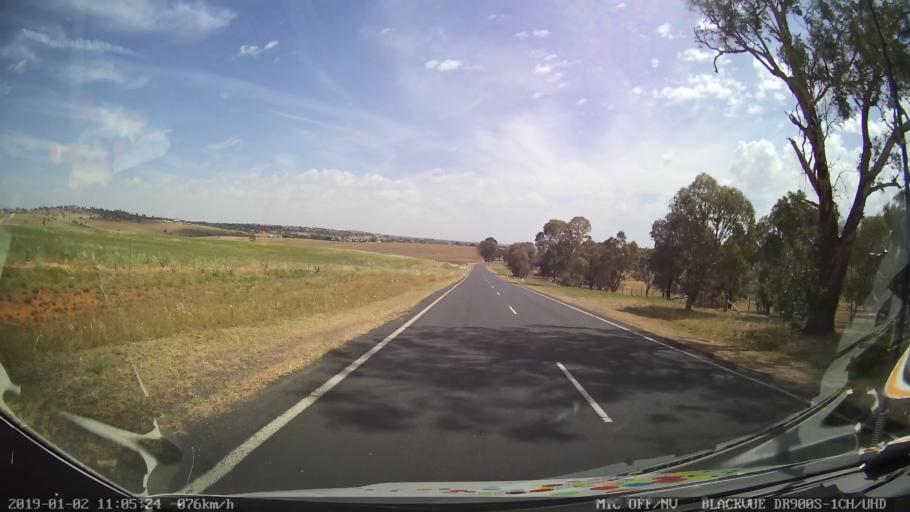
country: AU
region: New South Wales
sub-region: Young
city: Young
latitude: -34.5652
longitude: 148.3540
